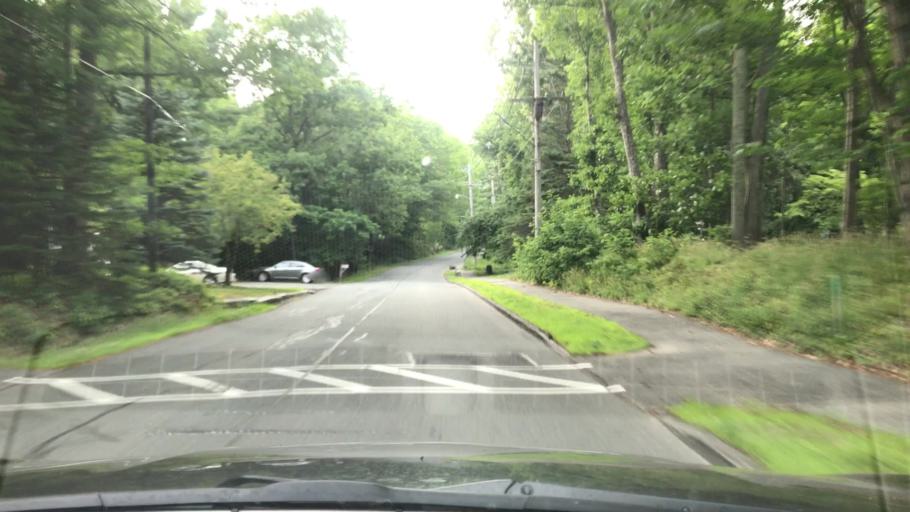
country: US
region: Maine
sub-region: Hancock County
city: Bar Harbor
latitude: 44.3691
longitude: -68.1957
